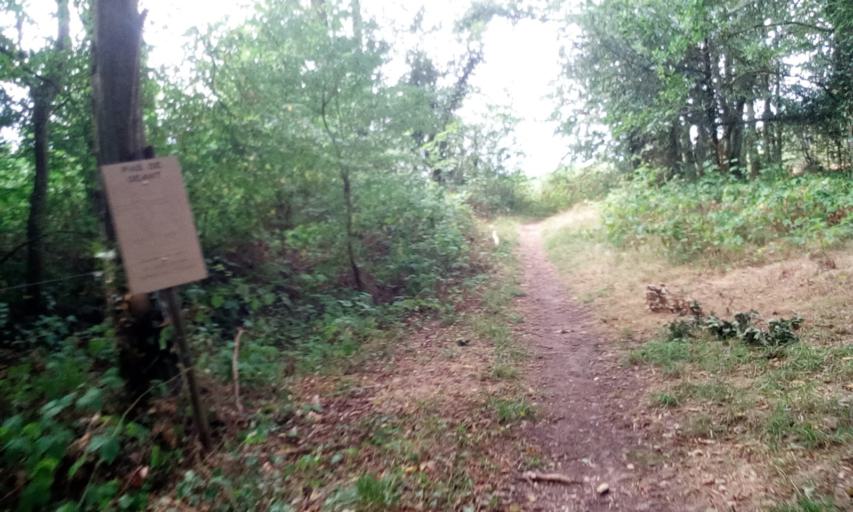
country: FR
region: Lower Normandy
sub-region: Departement du Calvados
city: Mouen
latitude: 49.1345
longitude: -0.4804
